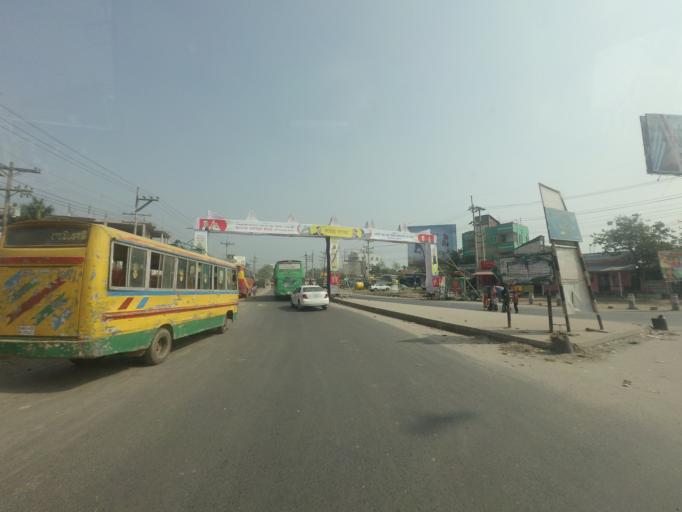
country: BD
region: Dhaka
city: Narsingdi
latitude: 23.9100
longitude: 90.6877
